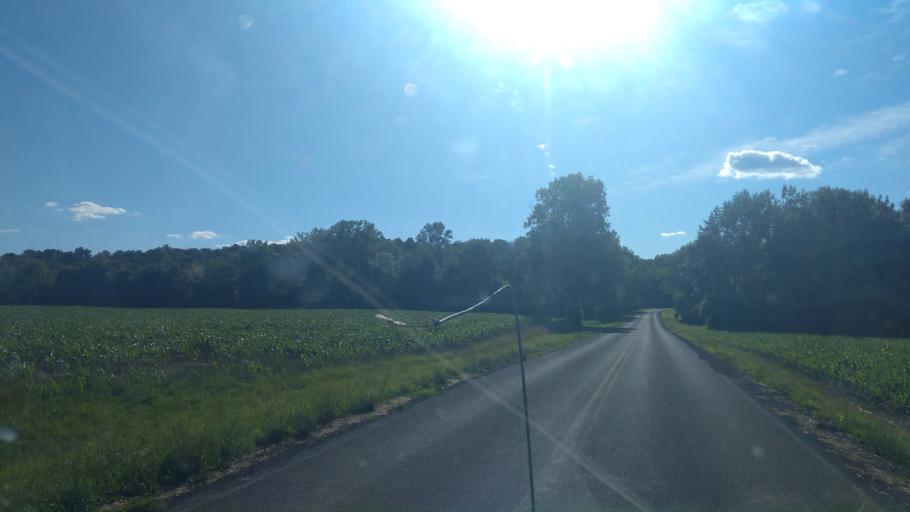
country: US
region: New York
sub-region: Wayne County
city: Lyons
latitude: 43.0038
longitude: -76.9650
